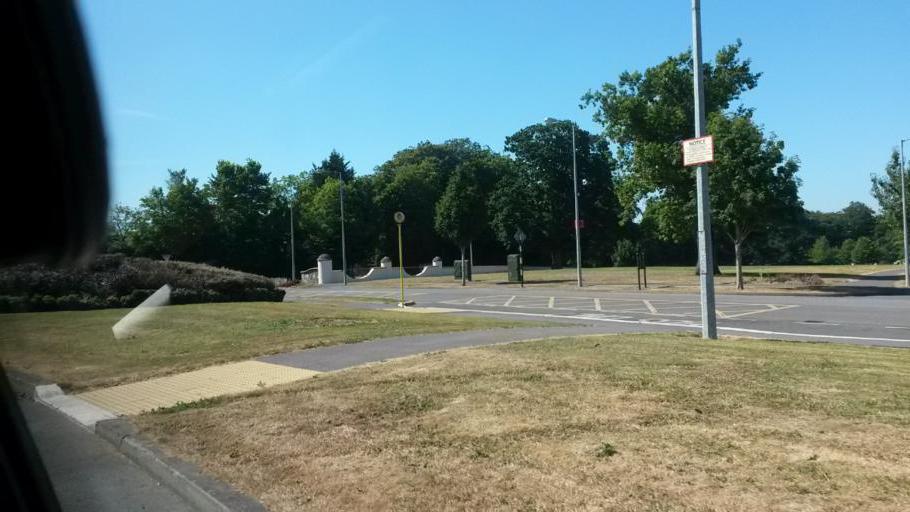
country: IE
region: Leinster
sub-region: Fingal County
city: Swords
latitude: 53.4546
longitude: -6.2640
